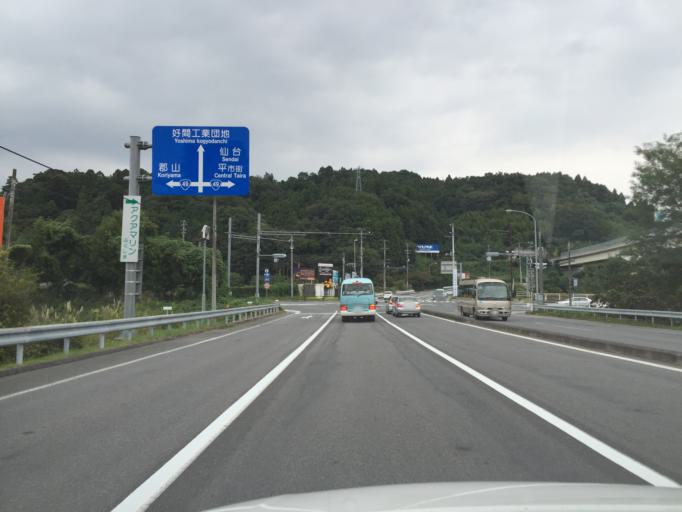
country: JP
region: Fukushima
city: Iwaki
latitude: 37.0699
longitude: 140.8396
